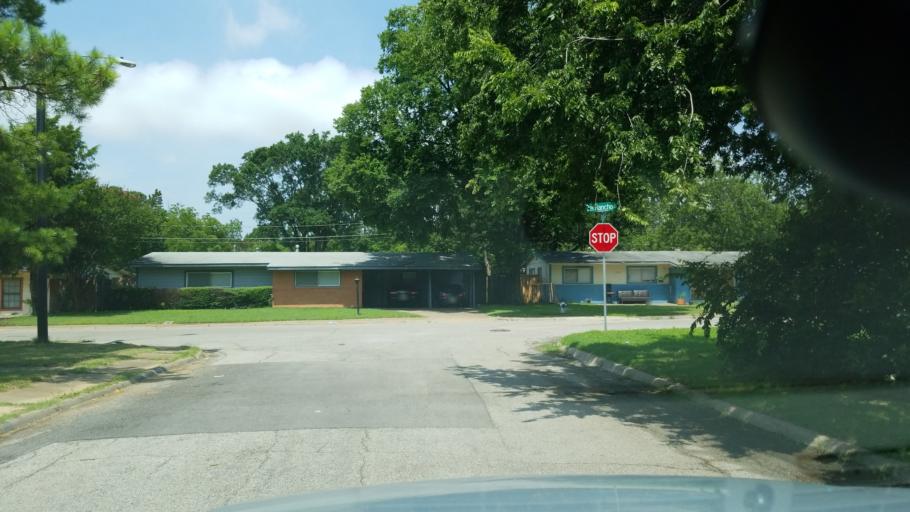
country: US
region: Texas
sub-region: Dallas County
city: Irving
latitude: 32.8321
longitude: -96.9478
